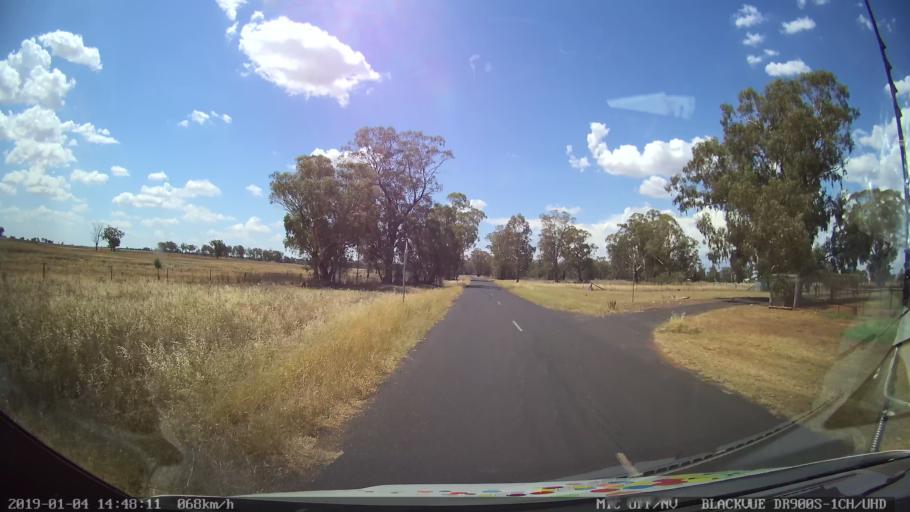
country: AU
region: New South Wales
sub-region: Dubbo Municipality
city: Dubbo
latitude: -32.0617
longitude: 148.6629
